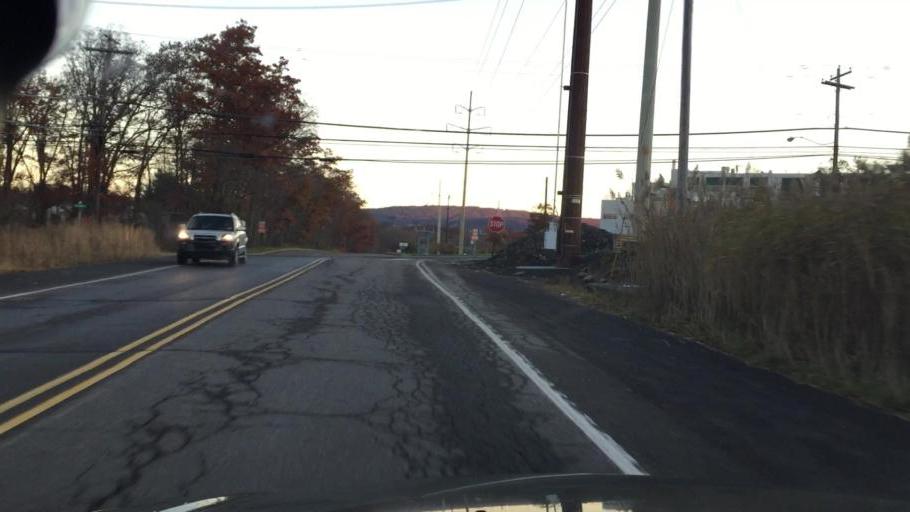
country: US
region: Pennsylvania
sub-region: Luzerne County
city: Mountain Top
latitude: 41.1417
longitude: -75.8963
